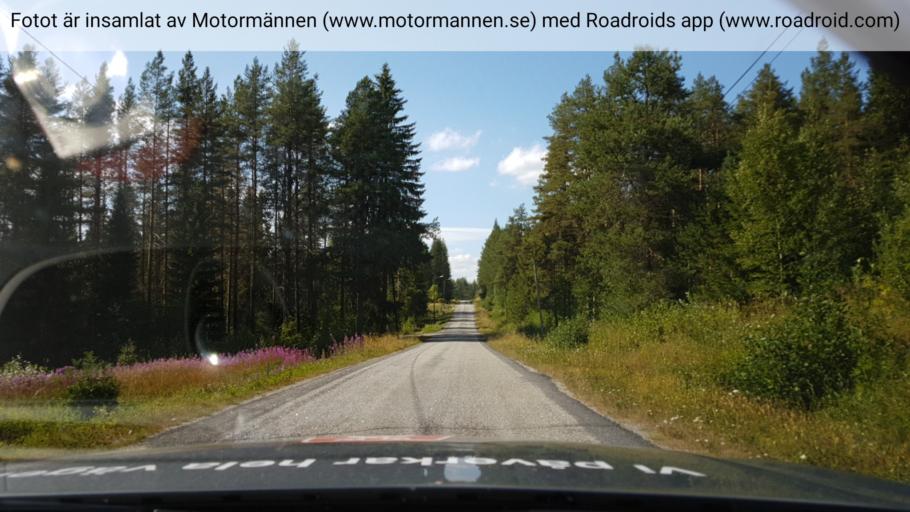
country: SE
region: Vaesterbotten
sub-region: Dorotea Kommun
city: Dorotea
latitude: 64.0999
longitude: 16.4062
